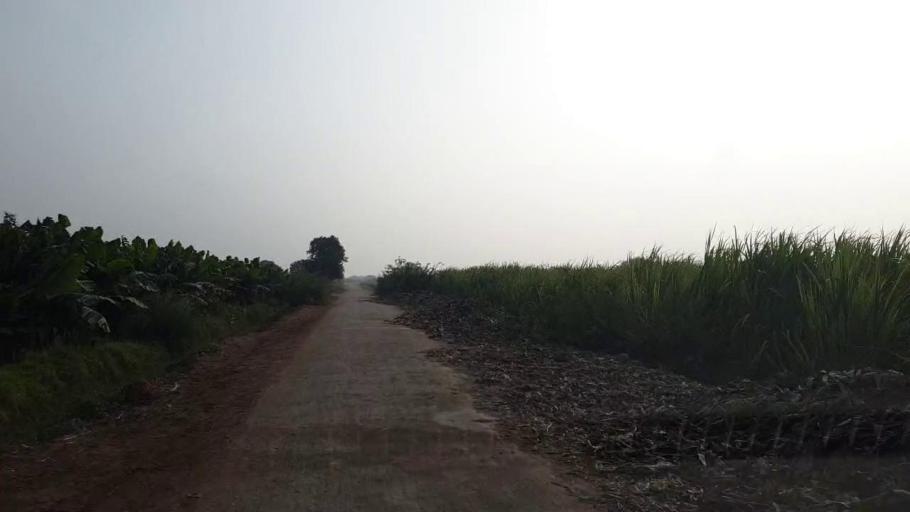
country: PK
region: Sindh
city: Tando Muhammad Khan
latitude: 25.1615
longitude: 68.5887
